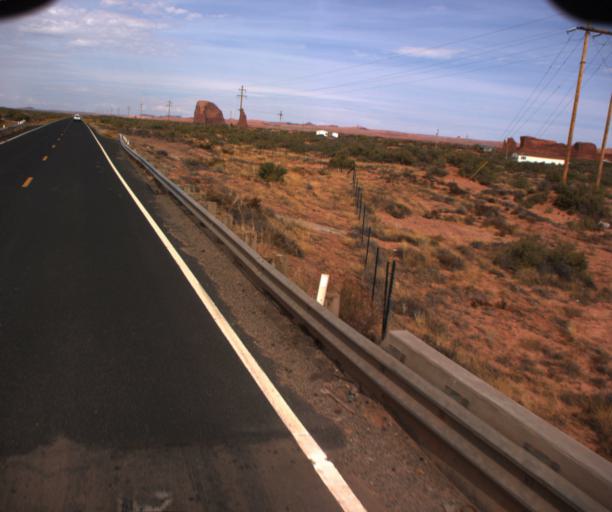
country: US
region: Arizona
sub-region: Apache County
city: Many Farms
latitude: 36.6274
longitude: -109.5839
